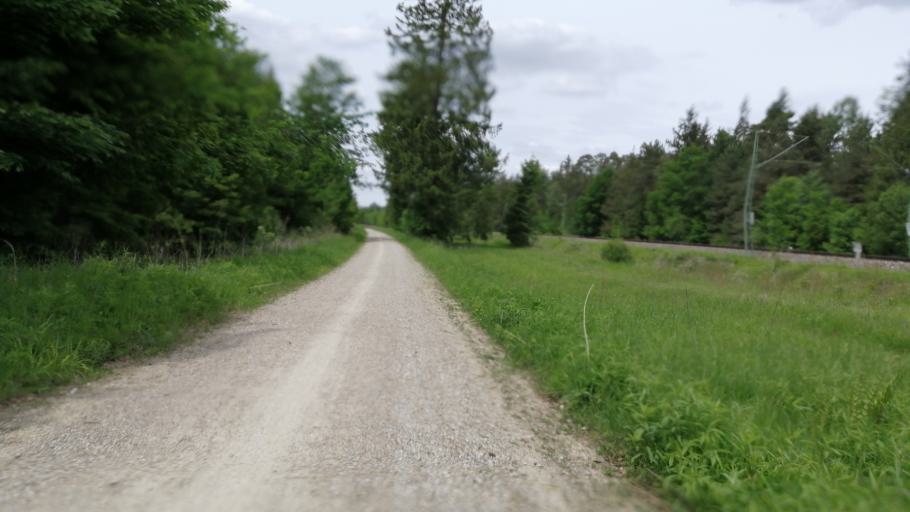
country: DE
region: Bavaria
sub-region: Upper Bavaria
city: Pullach im Isartal
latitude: 48.0659
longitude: 11.5613
